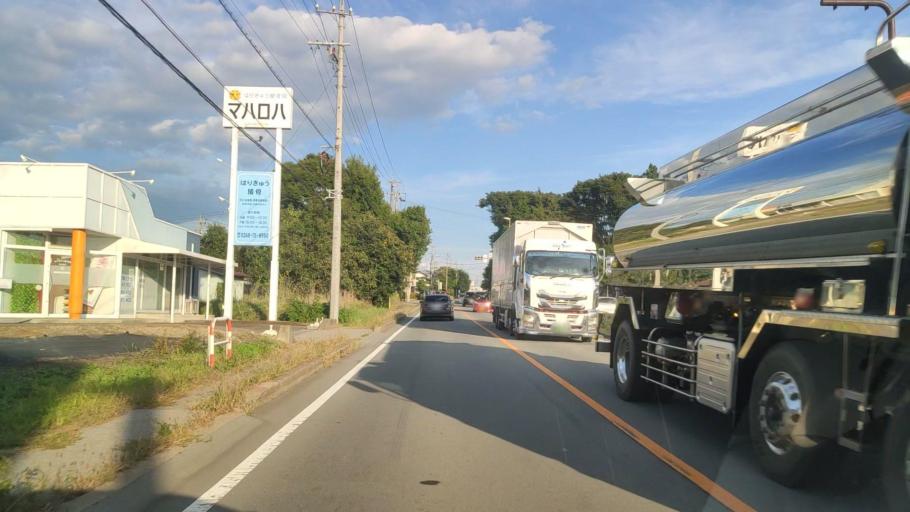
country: JP
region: Nagano
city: Ueda
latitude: 36.3556
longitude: 138.3416
